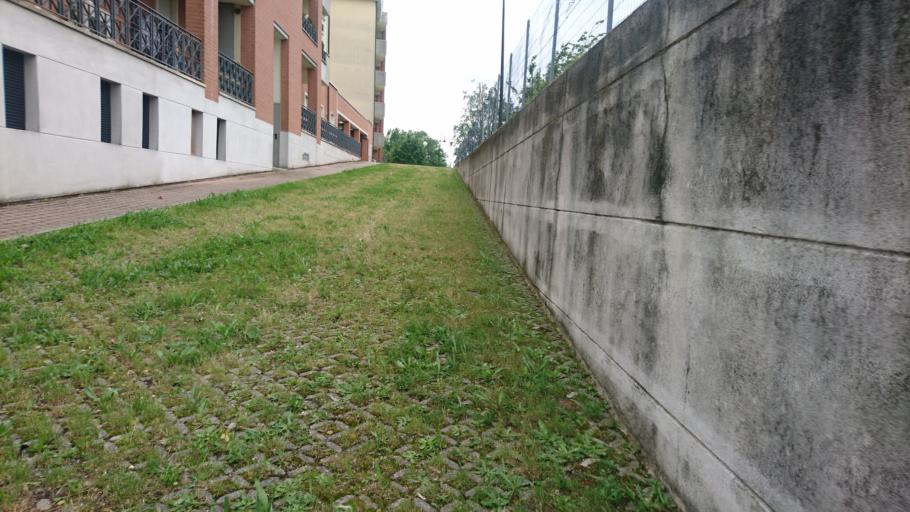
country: IT
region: Veneto
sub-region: Provincia di Padova
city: Padova
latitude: 45.3973
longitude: 11.9074
